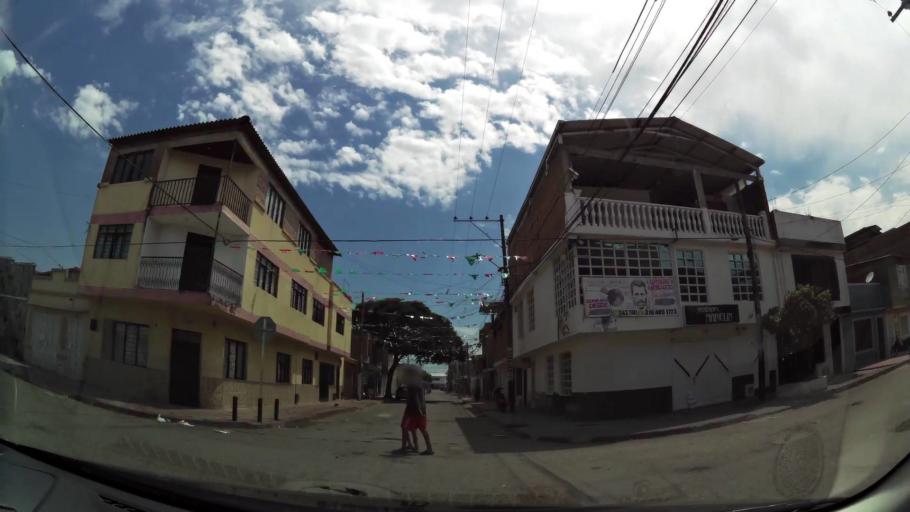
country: CO
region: Valle del Cauca
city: Cali
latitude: 3.4405
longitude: -76.5174
